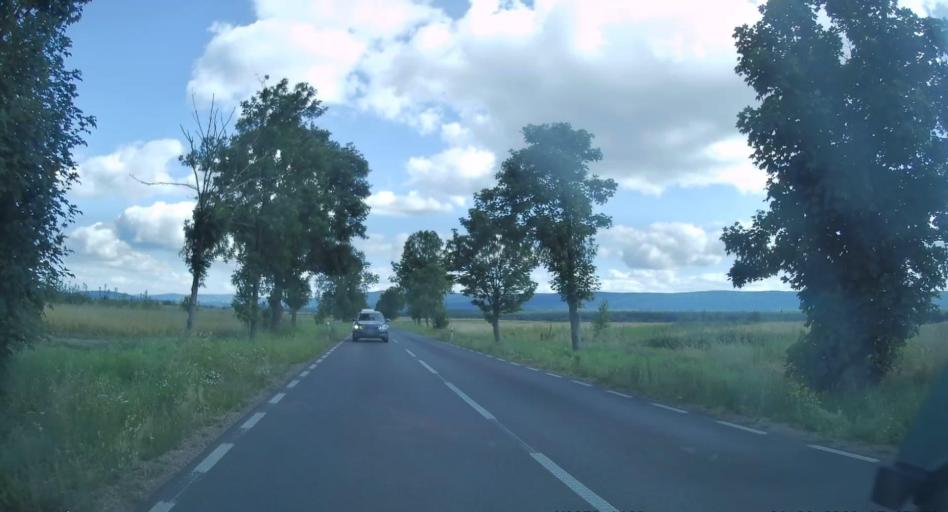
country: PL
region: Swietokrzyskie
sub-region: Powiat kielecki
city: Bodzentyn
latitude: 50.9287
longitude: 20.9810
